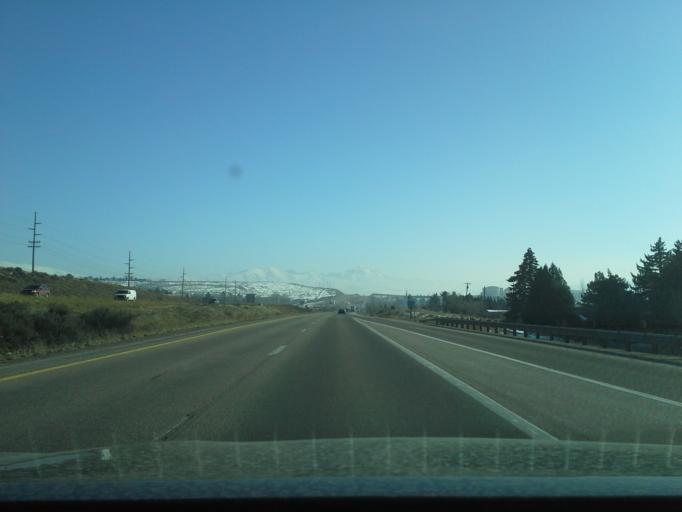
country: US
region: Idaho
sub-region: Bannock County
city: Pocatello
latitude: 42.8715
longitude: -112.4234
